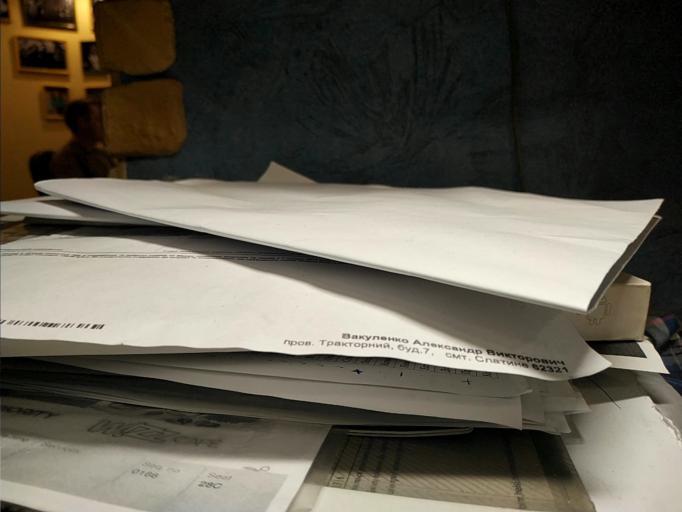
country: RU
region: Tverskaya
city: Zubtsov
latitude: 56.1198
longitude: 34.5755
